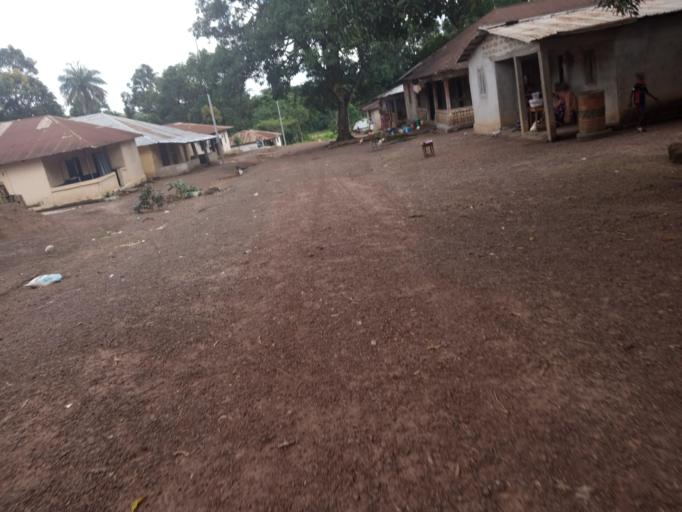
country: SL
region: Northern Province
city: Kamakwie
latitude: 9.4939
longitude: -12.2411
